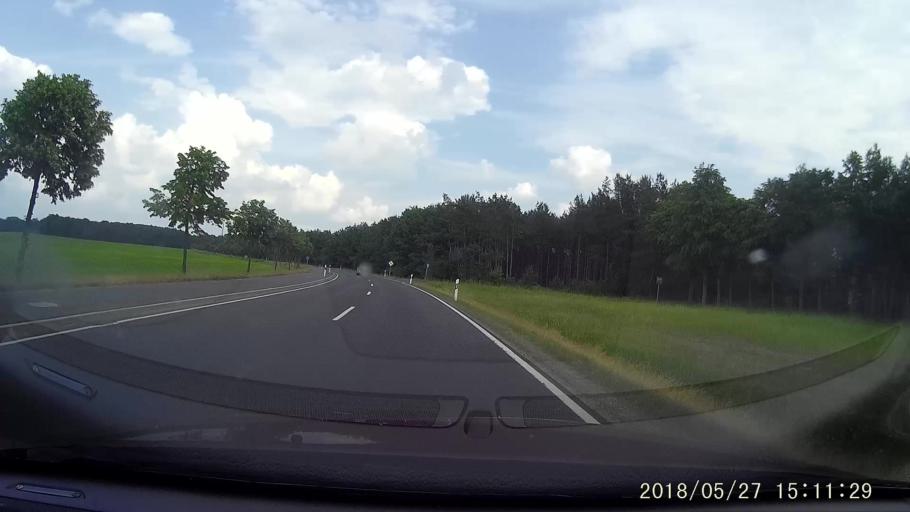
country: DE
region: Saxony
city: Quitzdorf
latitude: 51.2930
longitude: 14.7900
